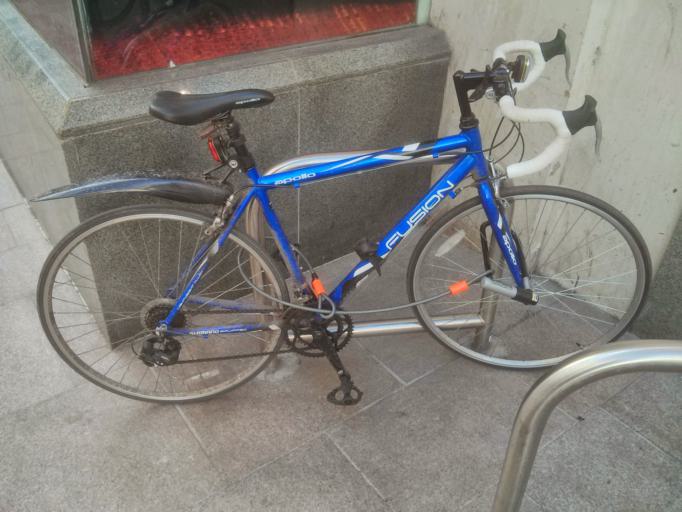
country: GB
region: England
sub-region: City and Borough of Leeds
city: Leeds
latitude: 53.7937
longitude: -1.5438
